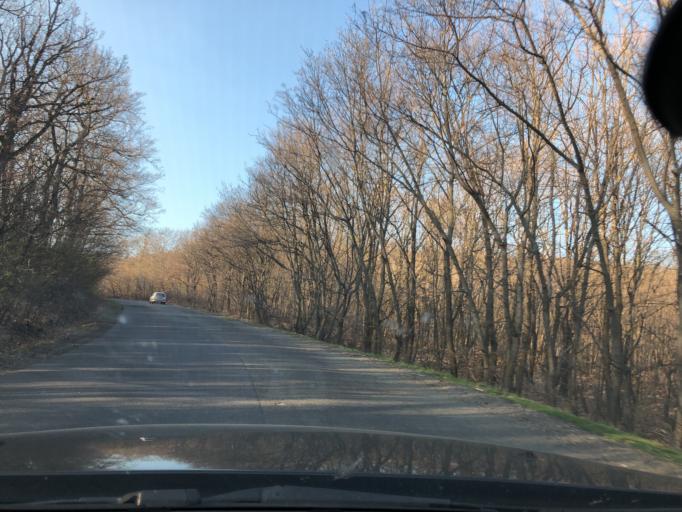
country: HU
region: Nograd
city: Paszto
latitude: 47.9221
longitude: 19.6318
